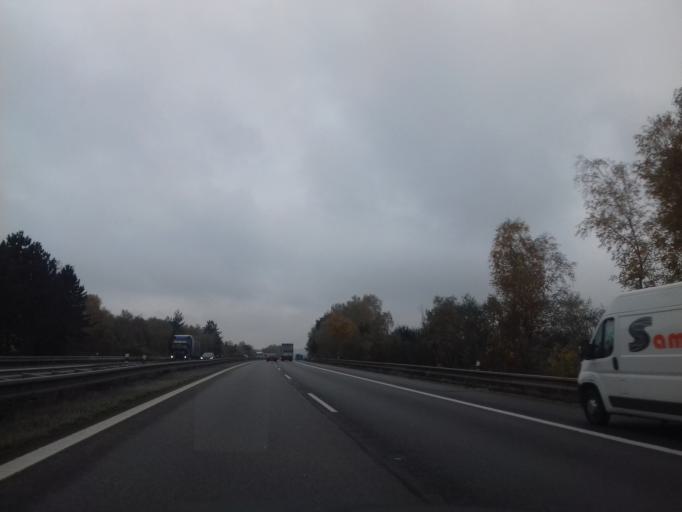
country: CZ
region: Vysocina
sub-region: Okres Pelhrimov
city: Zeliv
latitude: 49.5906
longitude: 15.2457
